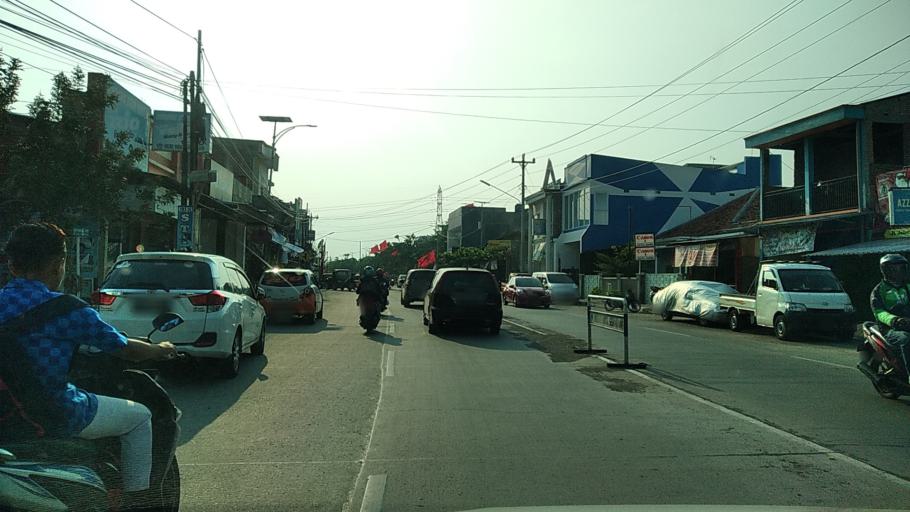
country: ID
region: Central Java
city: Semarang
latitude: -6.9857
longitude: 110.4464
